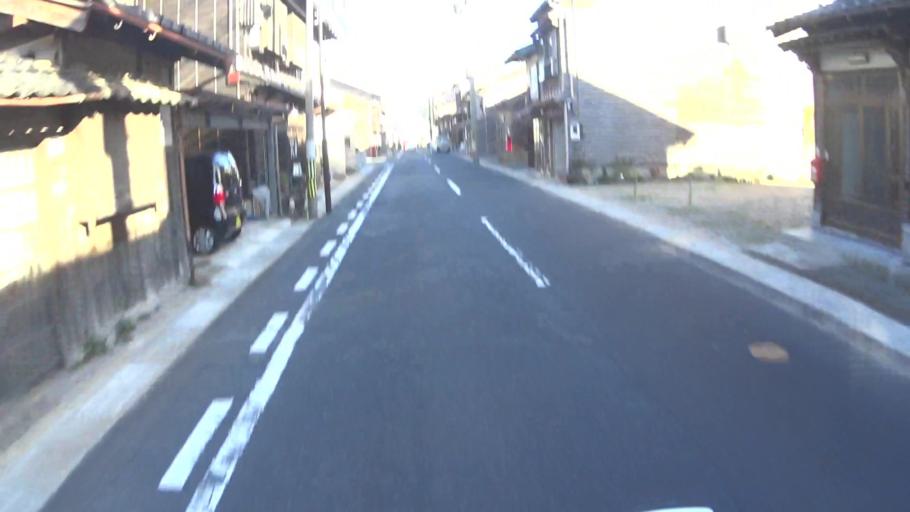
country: JP
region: Hyogo
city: Toyooka
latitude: 35.6064
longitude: 134.8948
